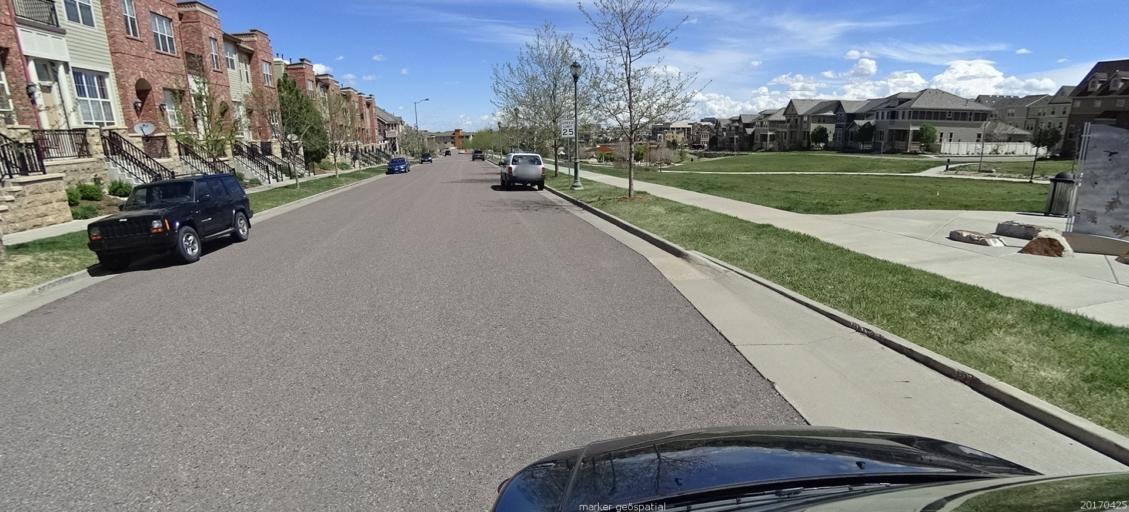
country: US
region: Colorado
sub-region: Douglas County
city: Carriage Club
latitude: 39.5286
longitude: -104.8815
